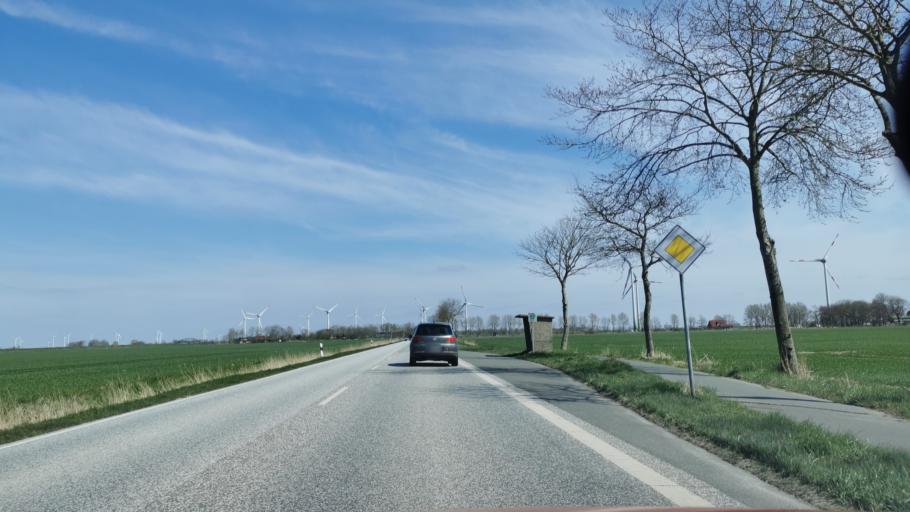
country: DE
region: Schleswig-Holstein
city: Friedrichsgabekoog
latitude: 54.1555
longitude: 8.9427
